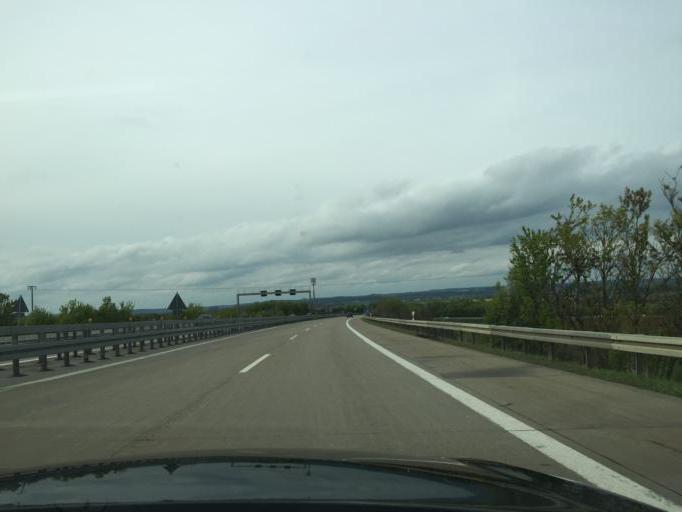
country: DE
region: Baden-Wuerttemberg
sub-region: Regierungsbezirk Stuttgart
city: Westhausen
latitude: 48.8797
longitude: 10.1651
